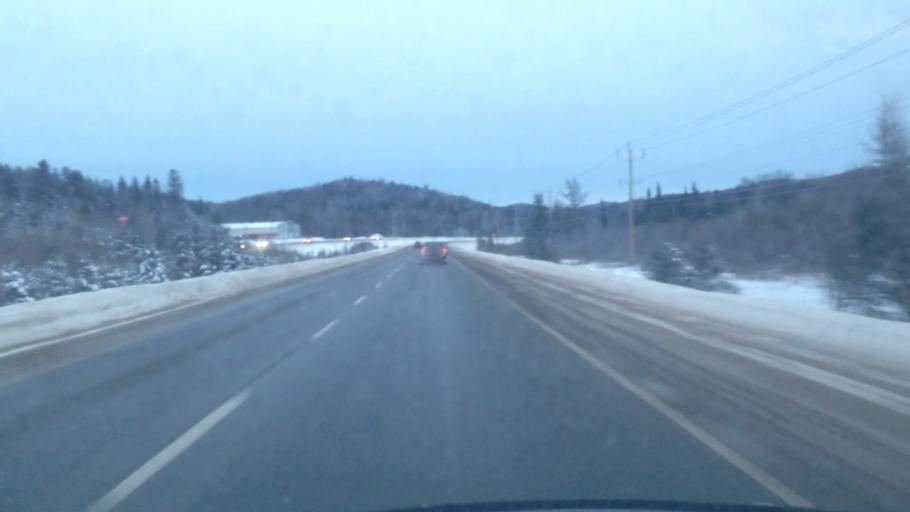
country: CA
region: Quebec
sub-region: Laurentides
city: Mont-Tremblant
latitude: 46.1122
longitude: -74.5261
